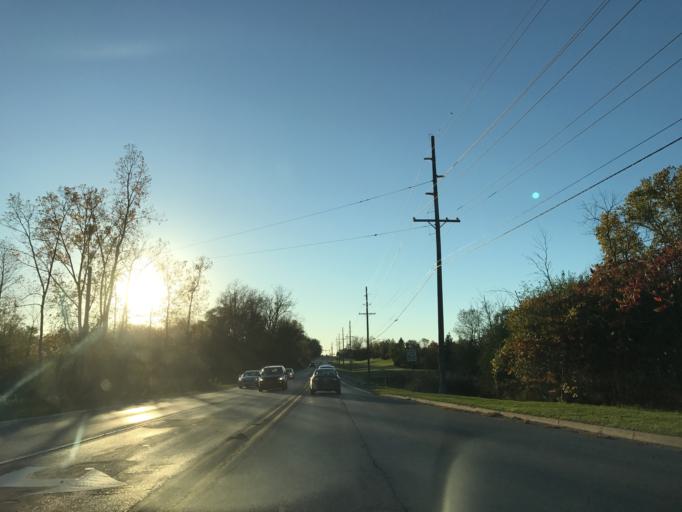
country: US
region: Michigan
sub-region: Oakland County
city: Wixom
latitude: 42.4648
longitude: -83.5342
